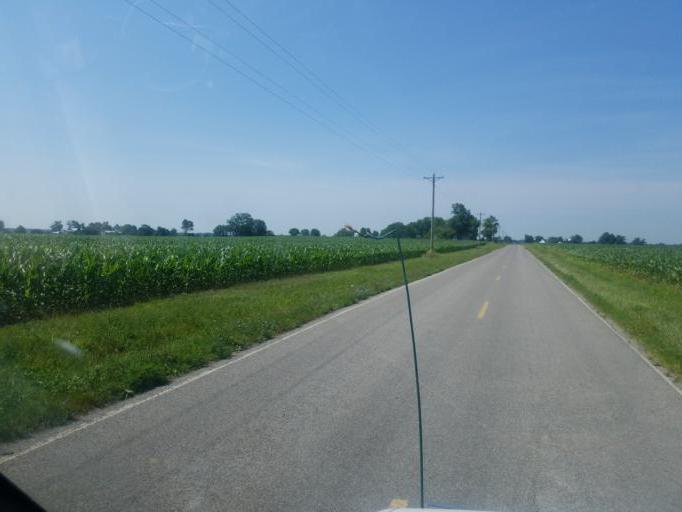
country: US
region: Ohio
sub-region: Champaign County
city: North Lewisburg
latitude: 40.1951
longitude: -83.5131
